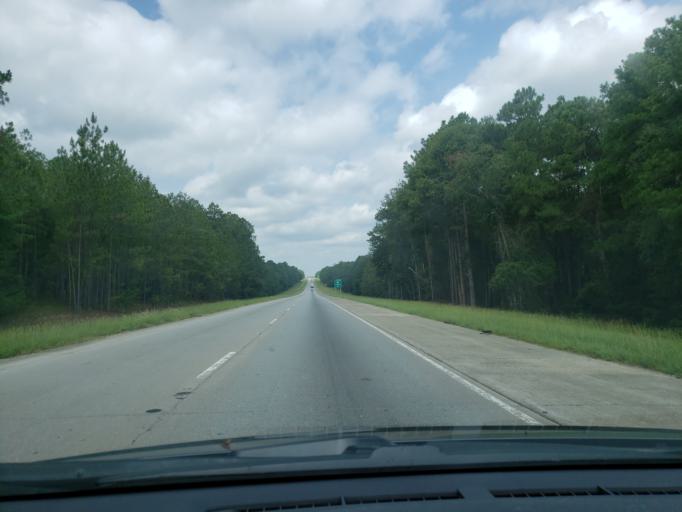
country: US
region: Georgia
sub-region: Emanuel County
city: Swainsboro
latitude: 32.4127
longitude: -82.3676
